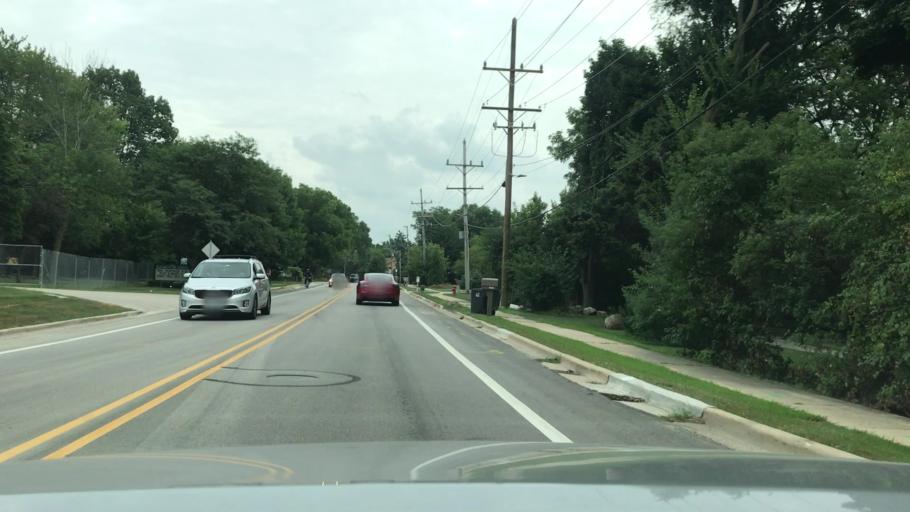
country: US
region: Illinois
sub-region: DuPage County
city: Darien
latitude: 41.7461
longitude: -87.9935
